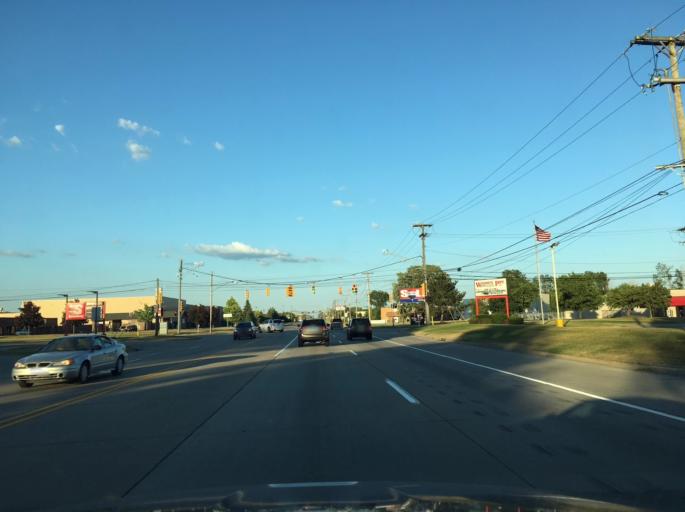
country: US
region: Michigan
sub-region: Macomb County
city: Fraser
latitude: 42.5540
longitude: -82.9314
